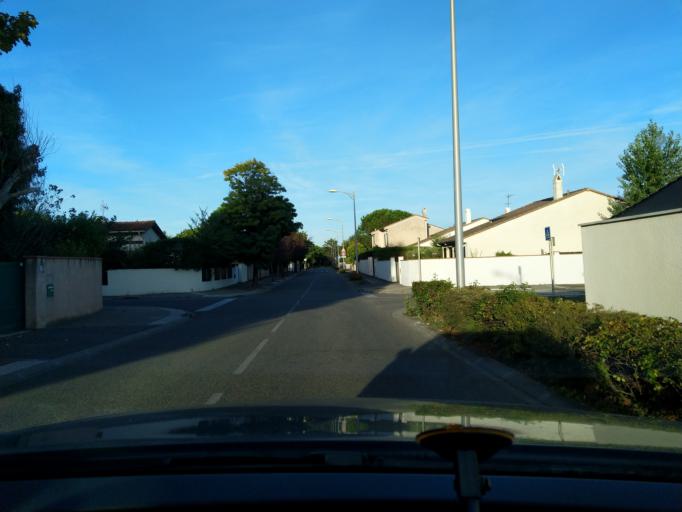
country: FR
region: Midi-Pyrenees
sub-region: Departement de la Haute-Garonne
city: Tournefeuille
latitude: 43.5771
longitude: 1.3298
